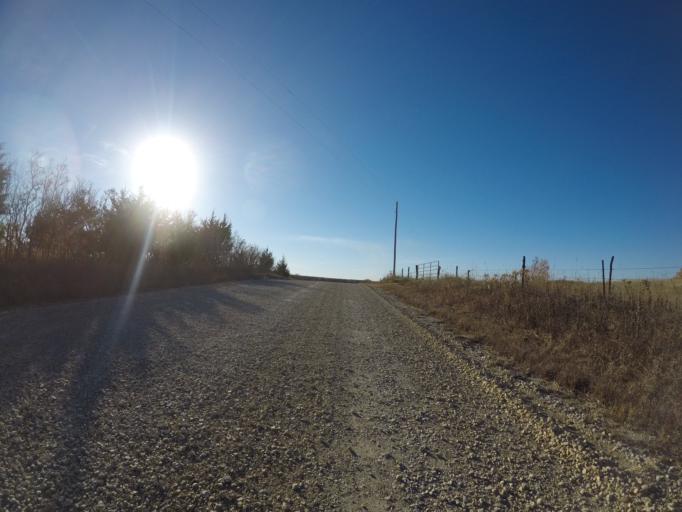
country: US
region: Kansas
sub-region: Riley County
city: Fort Riley North
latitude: 39.2620
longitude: -96.7739
